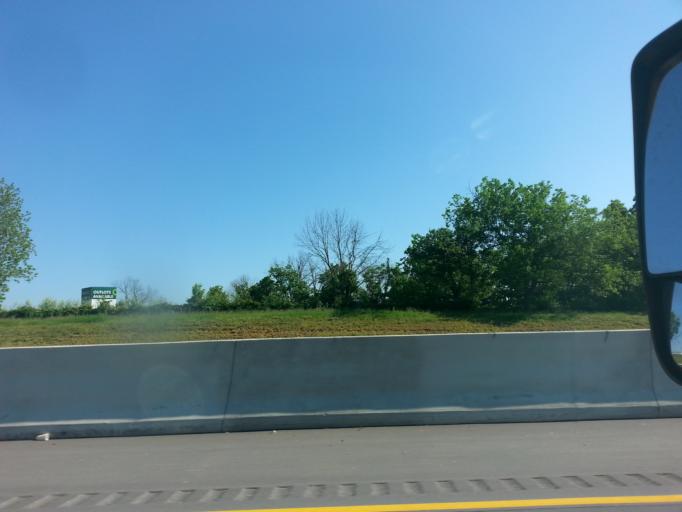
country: US
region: Kentucky
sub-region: Shelby County
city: Simpsonville
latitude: 38.2066
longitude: -85.3412
